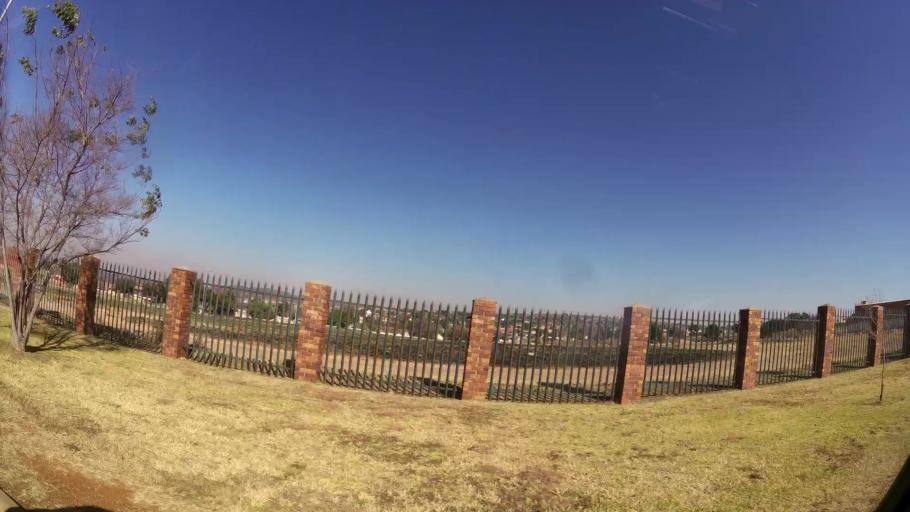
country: ZA
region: Gauteng
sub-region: Ekurhuleni Metropolitan Municipality
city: Germiston
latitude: -26.2495
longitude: 28.1134
